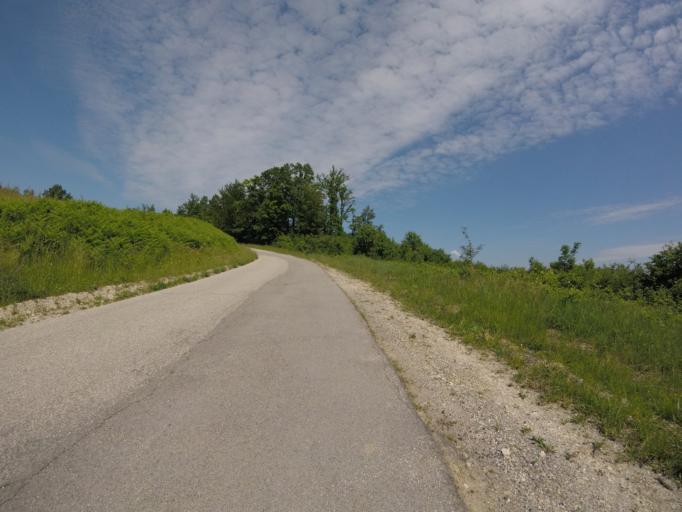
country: HR
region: Zagrebacka
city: Mraclin
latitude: 45.5756
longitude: 16.0100
